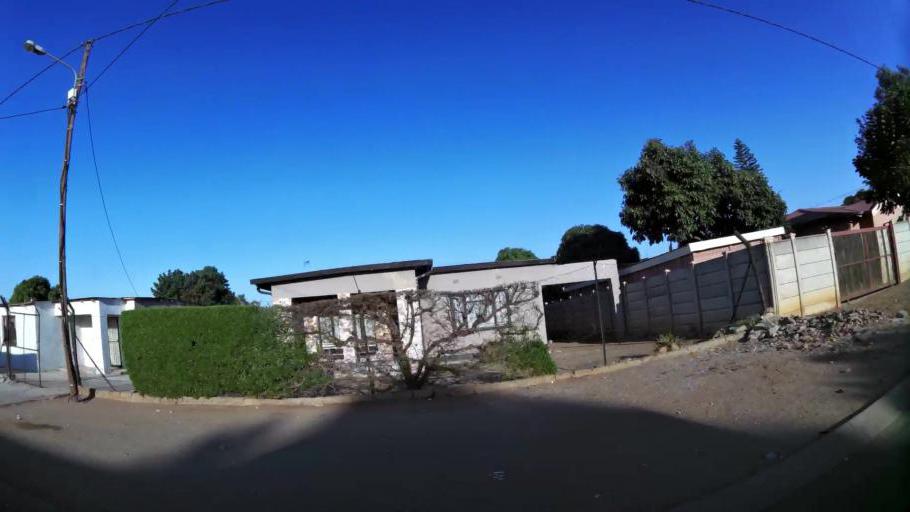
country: ZA
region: North-West
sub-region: Bojanala Platinum District Municipality
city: Rustenburg
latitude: -25.6429
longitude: 27.2165
